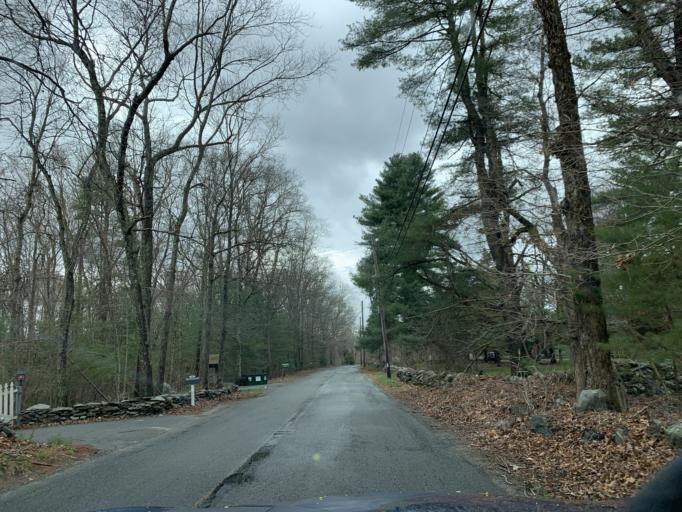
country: US
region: Massachusetts
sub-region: Bristol County
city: Rehoboth
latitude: 41.8867
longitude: -71.2079
